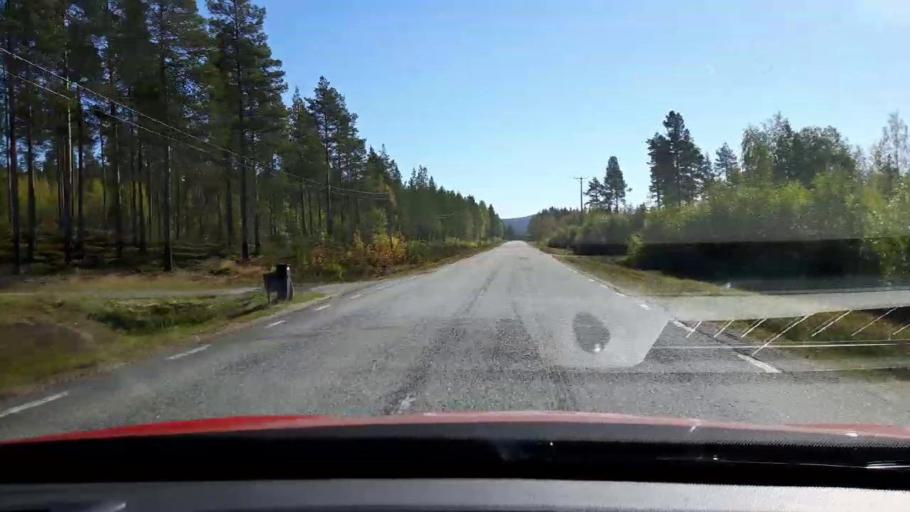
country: SE
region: Jaemtland
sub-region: Harjedalens Kommun
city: Sveg
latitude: 62.3006
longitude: 14.0644
